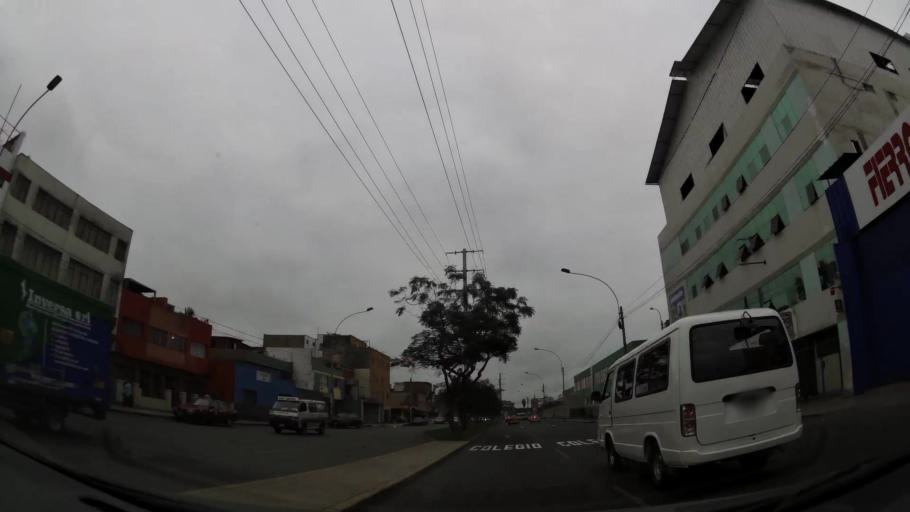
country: PE
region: Lima
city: Lima
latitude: -12.0528
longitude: -77.0611
